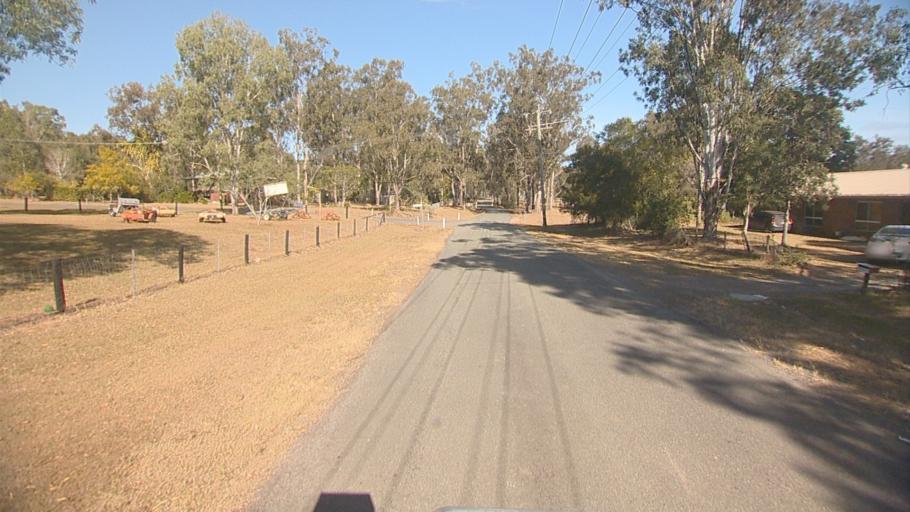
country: AU
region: Queensland
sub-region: Logan
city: Cedar Vale
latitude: -27.8573
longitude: 152.9809
